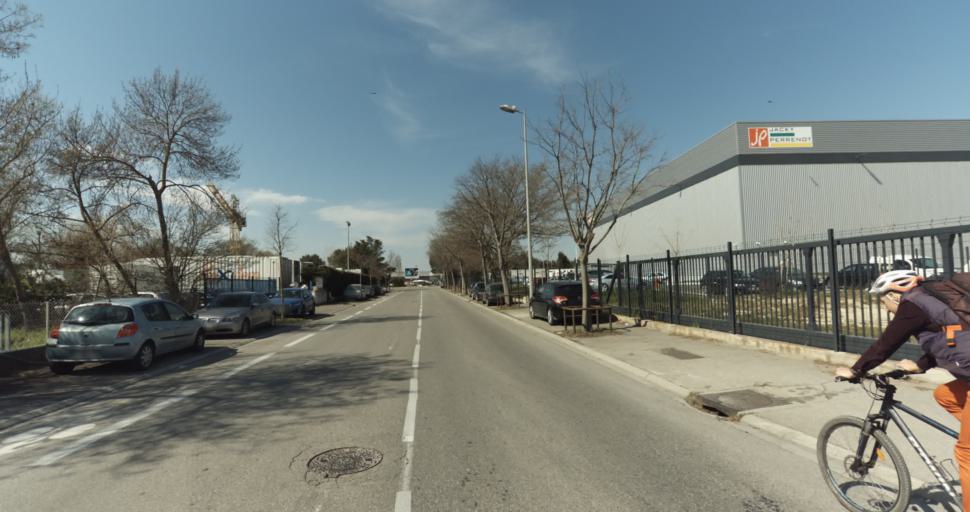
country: FR
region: Provence-Alpes-Cote d'Azur
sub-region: Departement des Bouches-du-Rhone
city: Cabries
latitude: 43.4876
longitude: 5.3718
